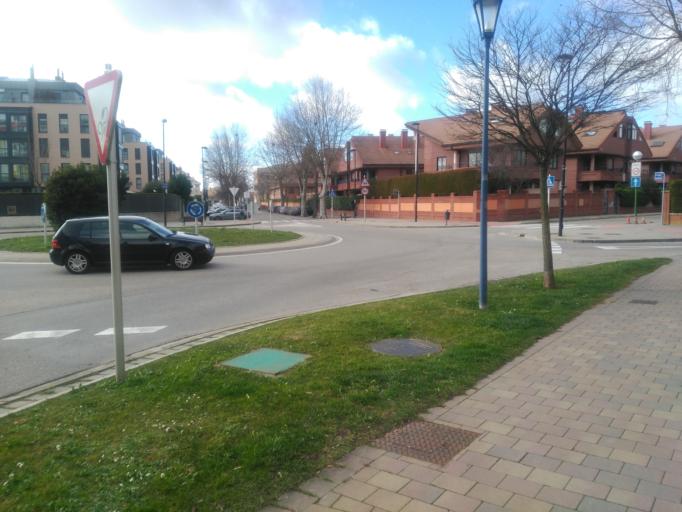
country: ES
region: Castille and Leon
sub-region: Provincia de Burgos
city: Burgos
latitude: 42.3359
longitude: -3.7116
